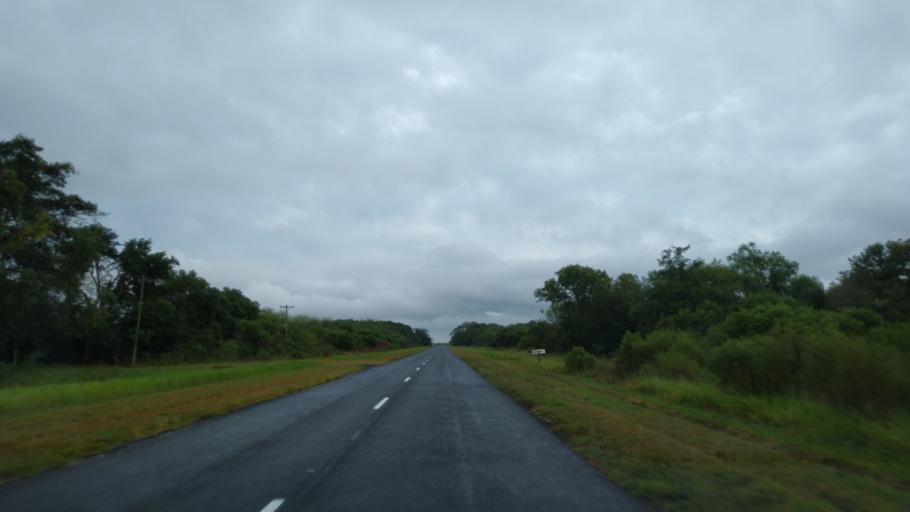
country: AR
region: Corrientes
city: Loreto
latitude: -27.7385
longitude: -57.2473
